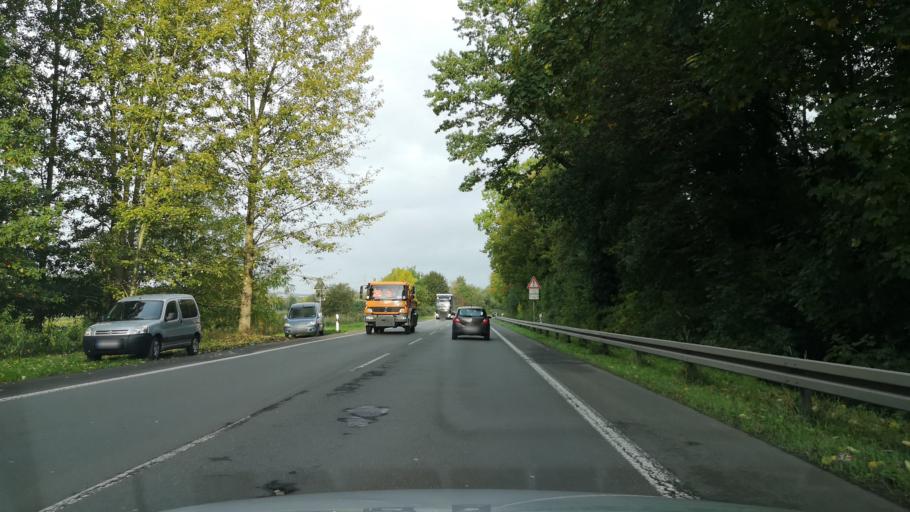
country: DE
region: North Rhine-Westphalia
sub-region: Regierungsbezirk Arnsberg
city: Hagen
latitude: 51.3934
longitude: 7.5144
